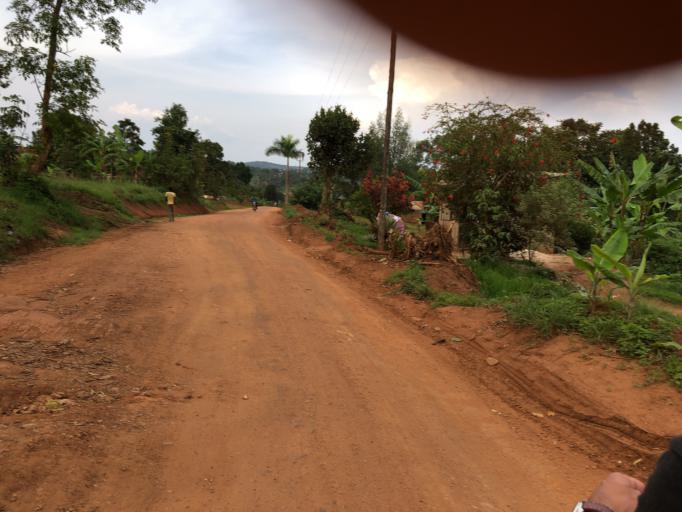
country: UG
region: Central Region
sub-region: Wakiso District
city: Bweyogerere
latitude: 0.4783
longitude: 32.6396
